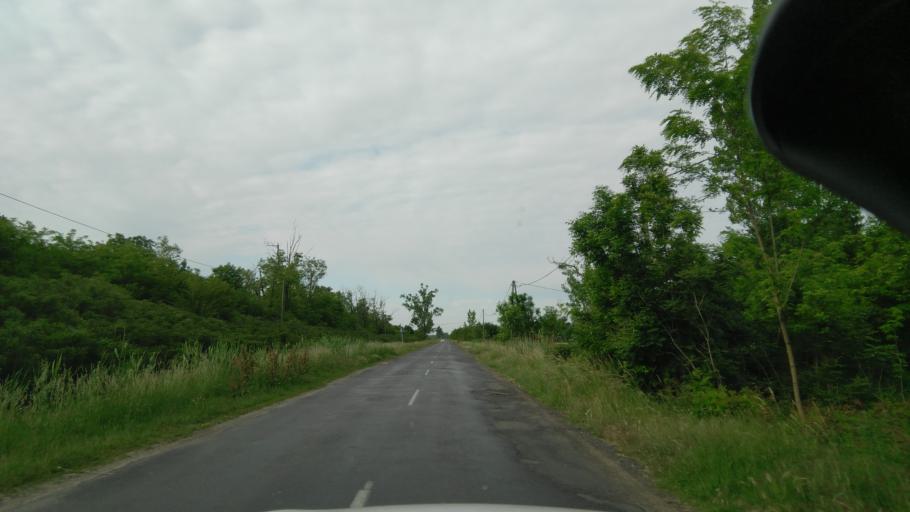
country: HU
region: Bekes
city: Elek
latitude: 46.5867
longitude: 21.2248
